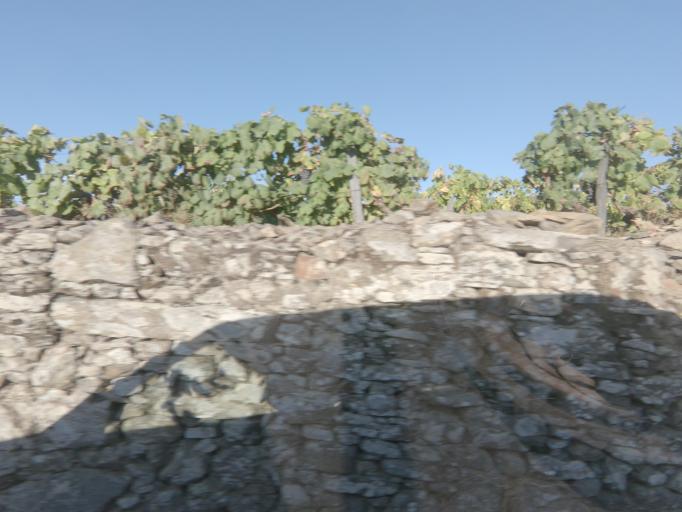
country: PT
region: Vila Real
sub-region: Peso da Regua
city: Godim
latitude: 41.1632
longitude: -7.8311
